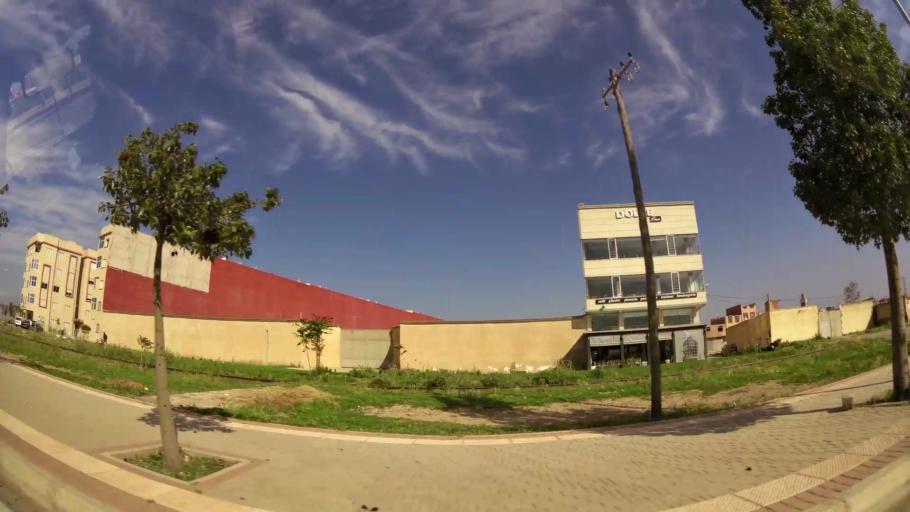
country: MA
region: Oriental
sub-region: Oujda-Angad
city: Oujda
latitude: 34.7152
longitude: -1.8840
